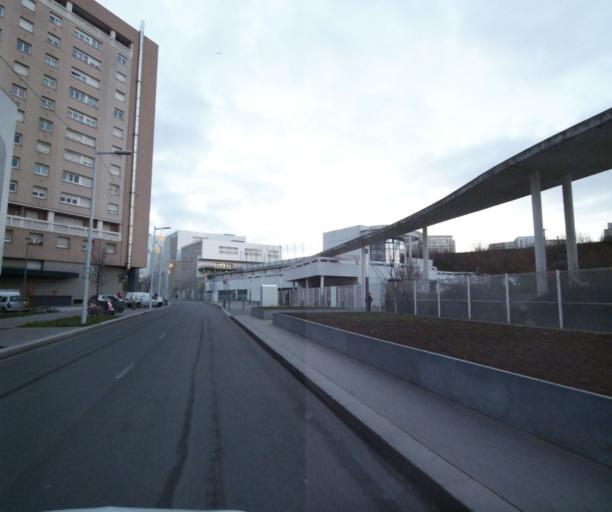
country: FR
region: Ile-de-France
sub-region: Departement des Hauts-de-Seine
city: Nanterre
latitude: 48.9026
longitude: 2.2068
